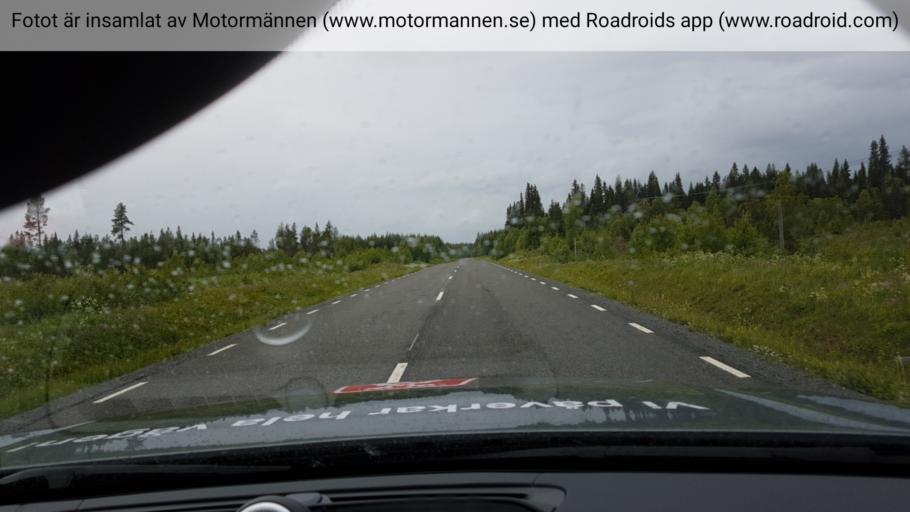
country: SE
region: Jaemtland
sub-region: Stroemsunds Kommun
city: Stroemsund
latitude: 63.6492
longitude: 15.1675
